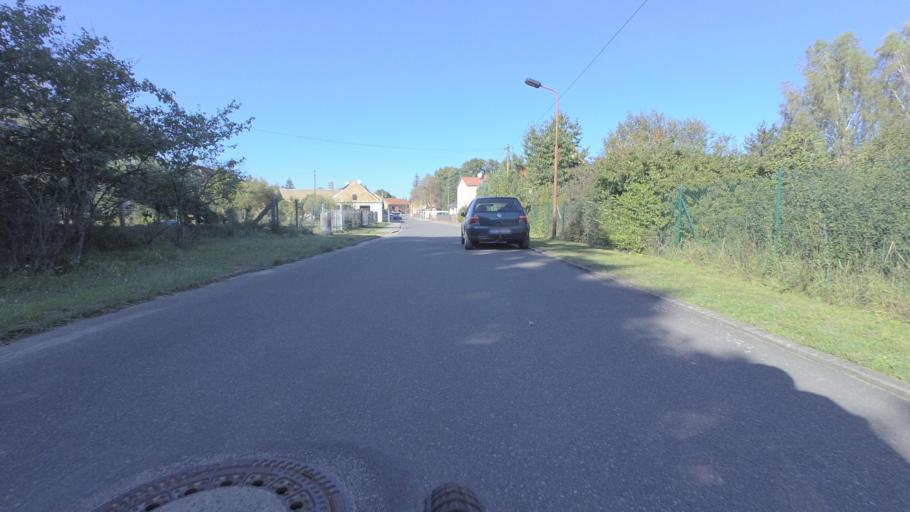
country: DE
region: Brandenburg
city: Sperenberg
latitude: 52.1544
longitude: 13.3409
